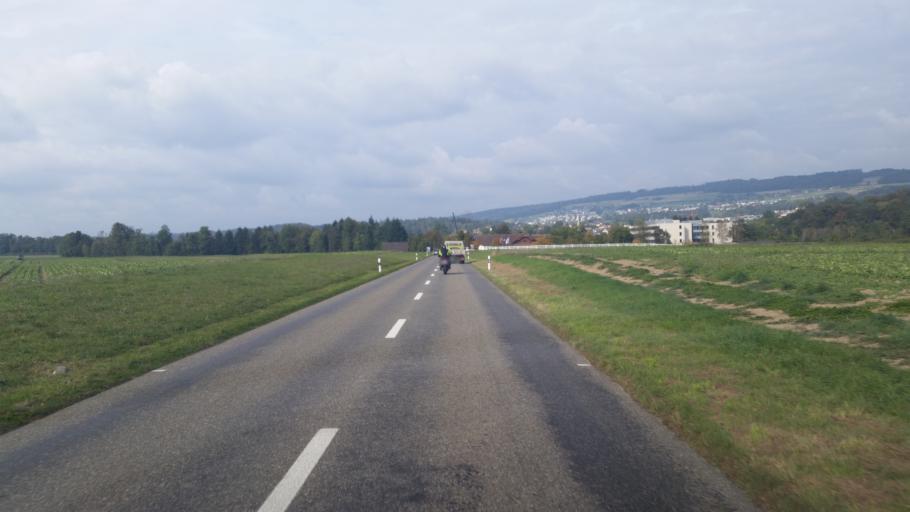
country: CH
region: Aargau
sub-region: Bezirk Baden
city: Kunten
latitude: 47.3882
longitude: 8.3024
